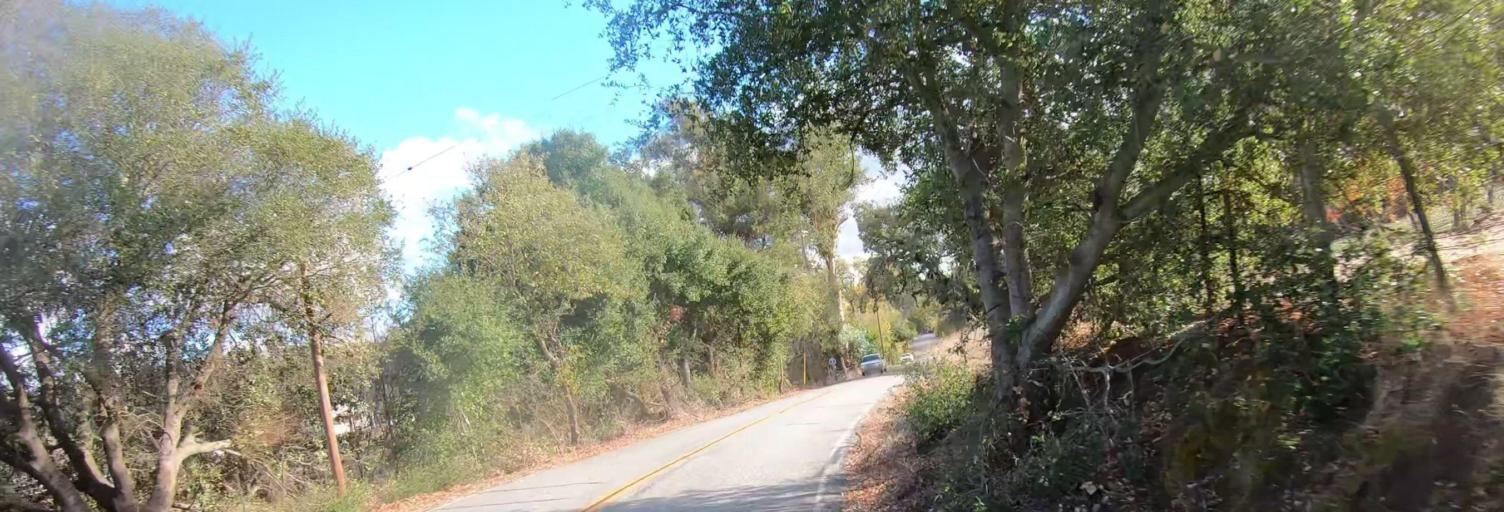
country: US
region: California
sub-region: Santa Clara County
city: East Foothills
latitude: 37.3462
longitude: -121.7261
